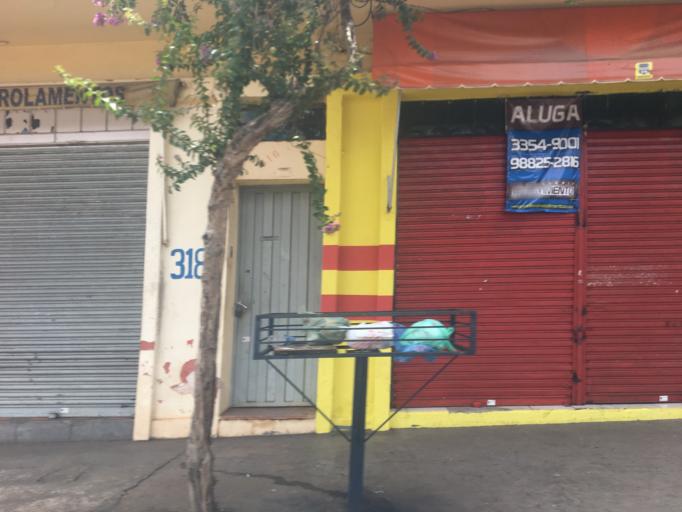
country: BR
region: Parana
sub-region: Londrina
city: Londrina
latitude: -23.3048
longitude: -51.1628
